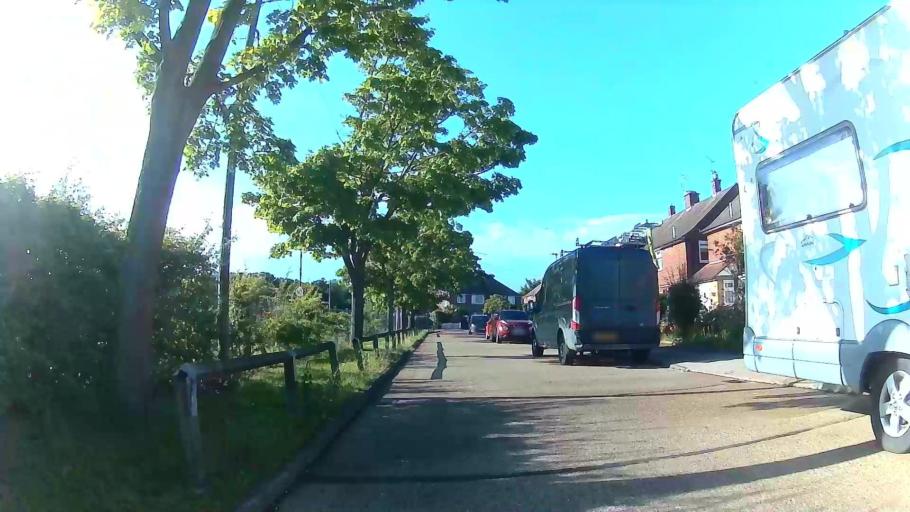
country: GB
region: England
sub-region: Essex
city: Chelmsford
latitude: 51.7508
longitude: 0.4512
